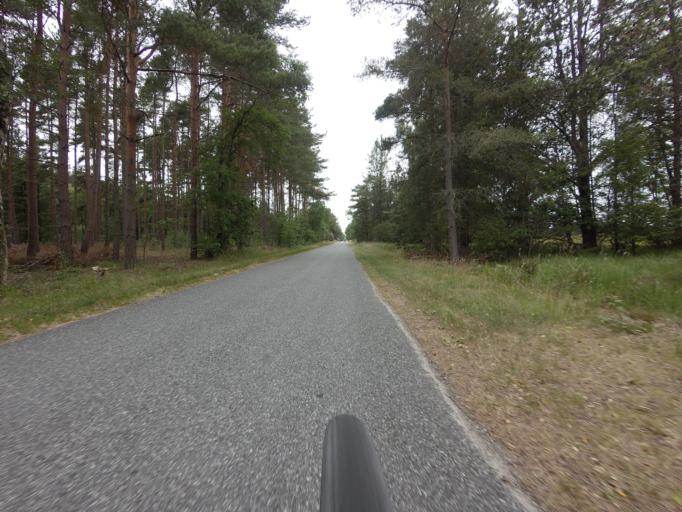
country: DK
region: North Denmark
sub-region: Laeso Kommune
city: Byrum
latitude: 57.2766
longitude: 10.9633
